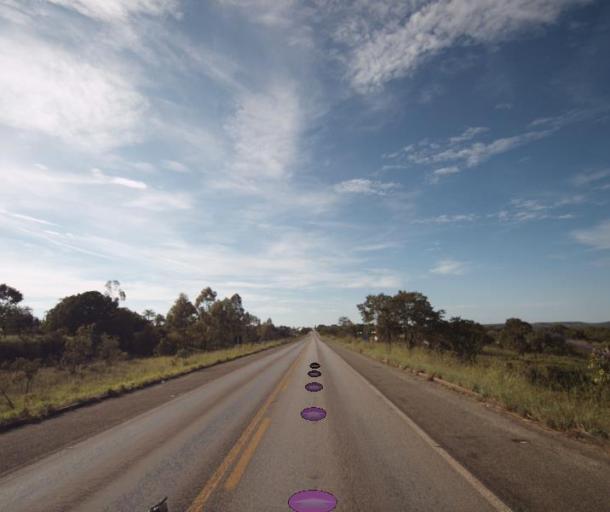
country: BR
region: Goias
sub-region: Pirenopolis
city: Pirenopolis
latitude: -15.7740
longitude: -48.5419
